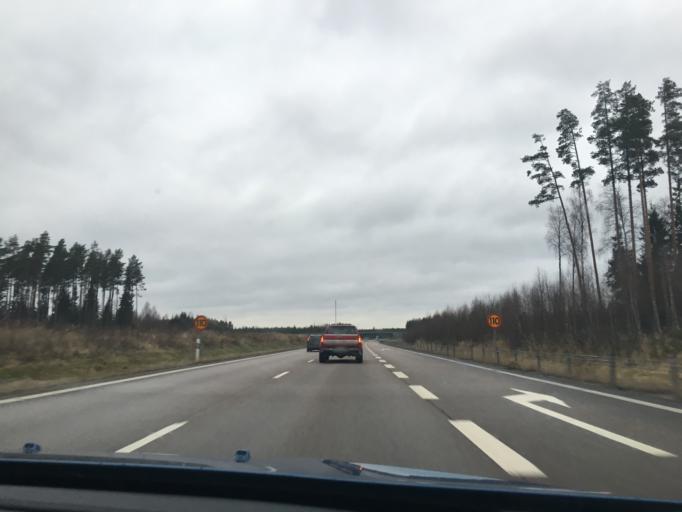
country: SE
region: Uppsala
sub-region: Tierps Kommun
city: Tierp
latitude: 60.4348
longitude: 17.4249
